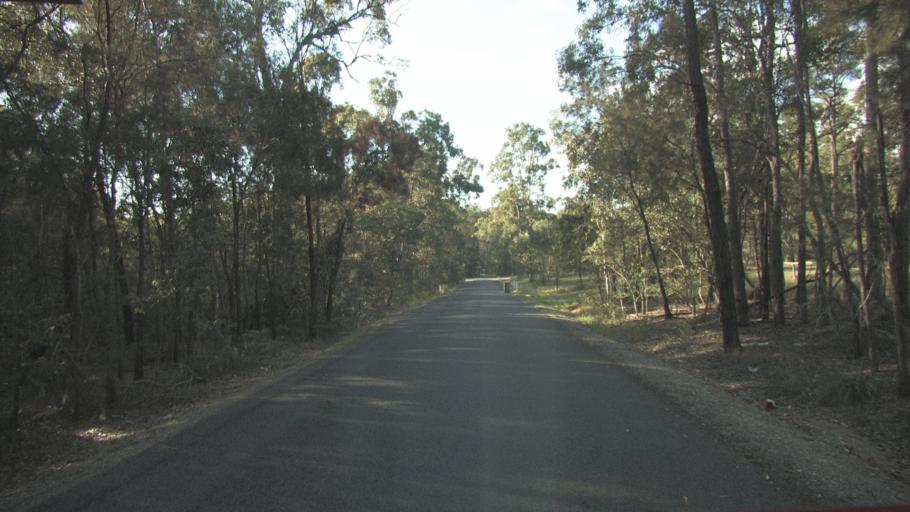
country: AU
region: Queensland
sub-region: Ipswich
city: Springfield Lakes
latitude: -27.6930
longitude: 152.9378
